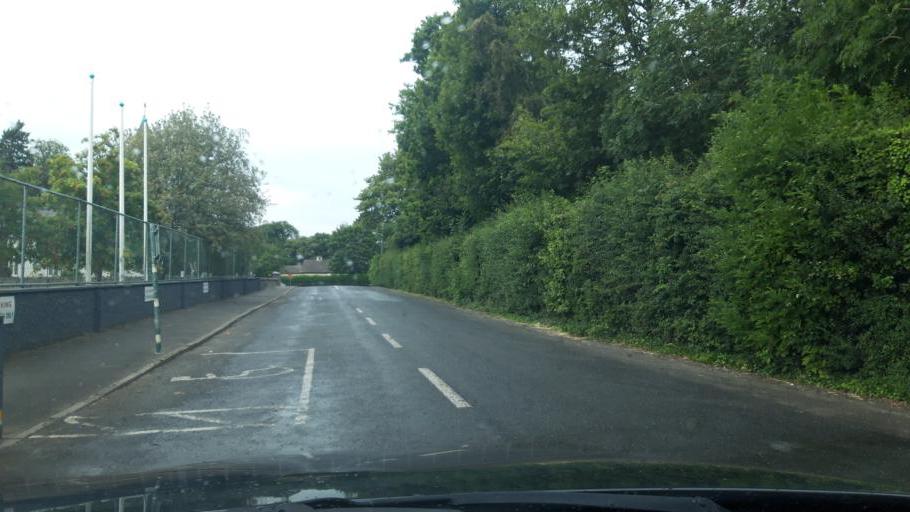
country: IE
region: Leinster
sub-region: Kildare
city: Cherryville
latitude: 53.1060
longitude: -7.0064
